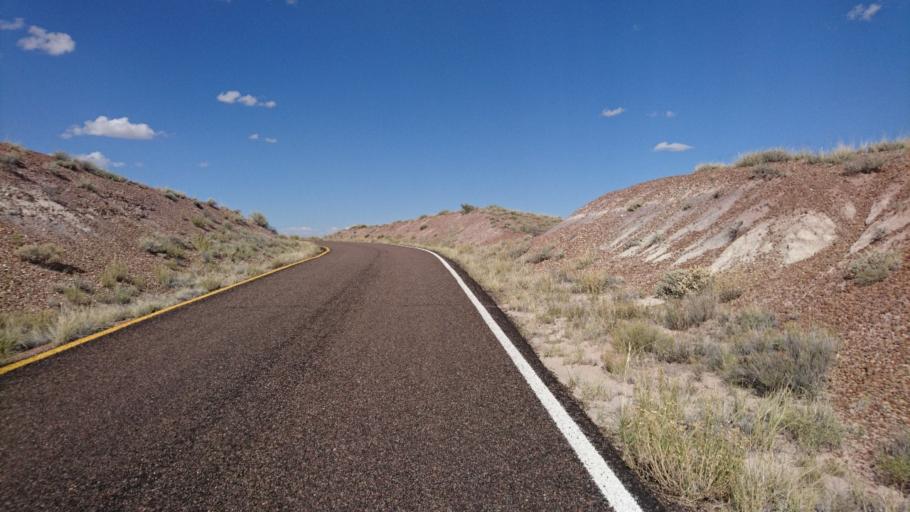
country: US
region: Arizona
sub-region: Navajo County
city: Holbrook
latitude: 34.8879
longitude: -109.8067
